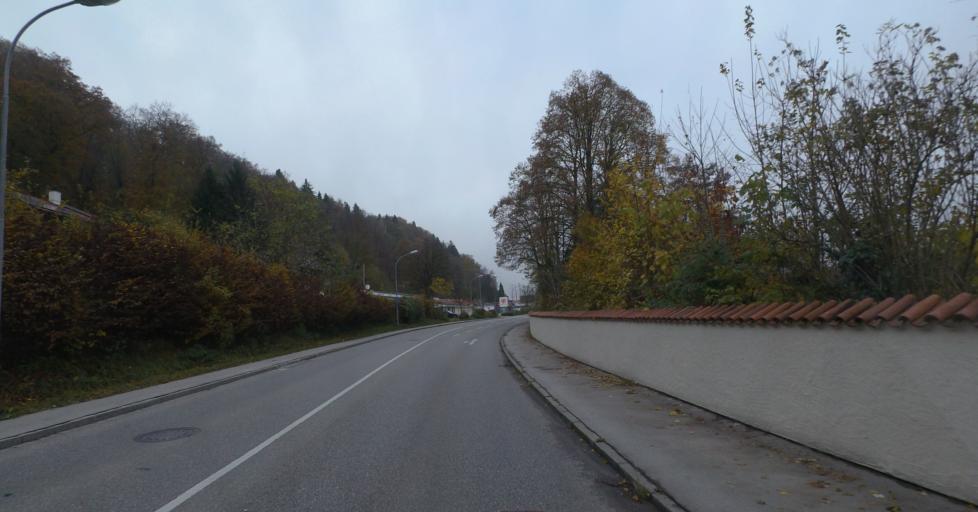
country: DE
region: Bavaria
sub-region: Upper Bavaria
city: Trostberg an der Alz
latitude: 48.0327
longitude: 12.5577
